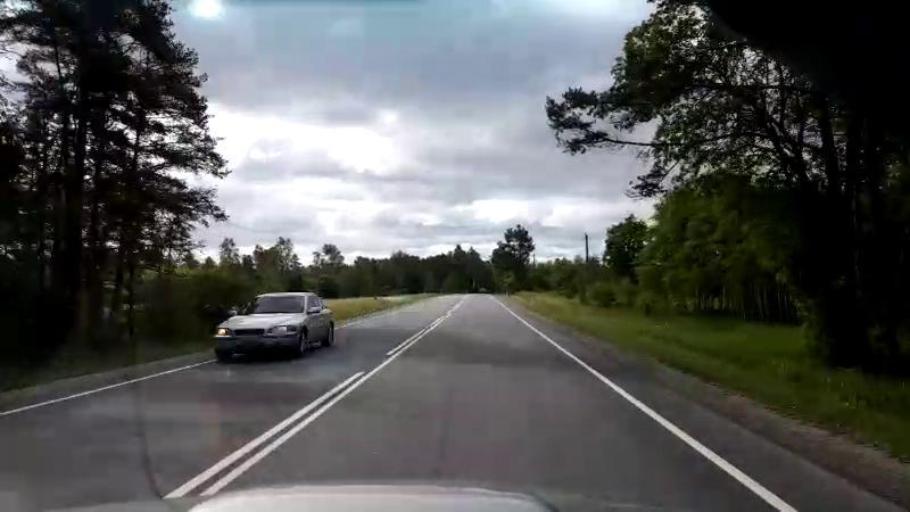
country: EE
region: Raplamaa
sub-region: Maerjamaa vald
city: Marjamaa
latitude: 58.9656
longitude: 24.4772
